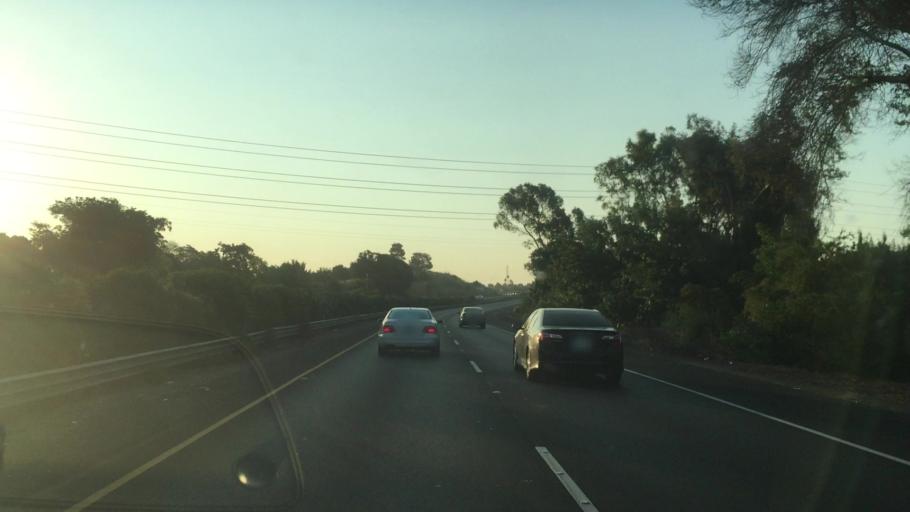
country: US
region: California
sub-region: Contra Costa County
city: Crockett
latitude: 38.0889
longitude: -122.2210
